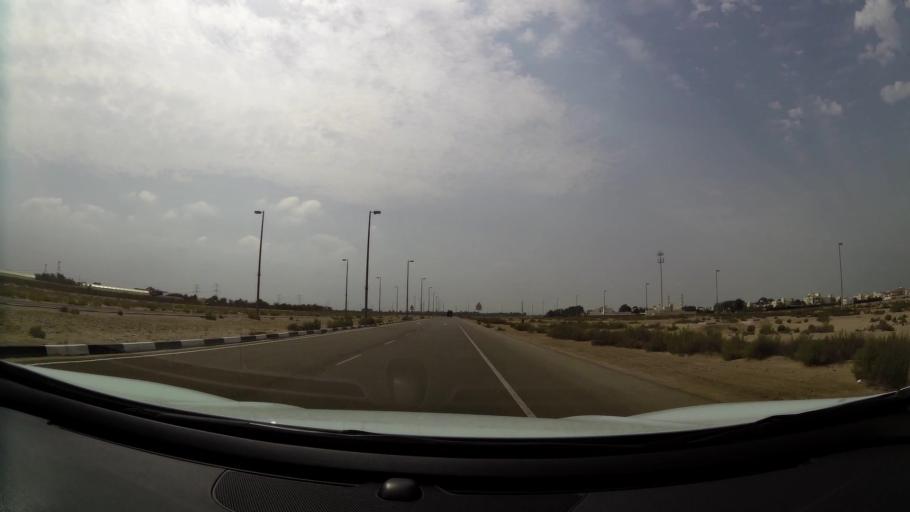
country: AE
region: Abu Dhabi
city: Abu Dhabi
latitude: 24.5798
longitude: 54.6503
